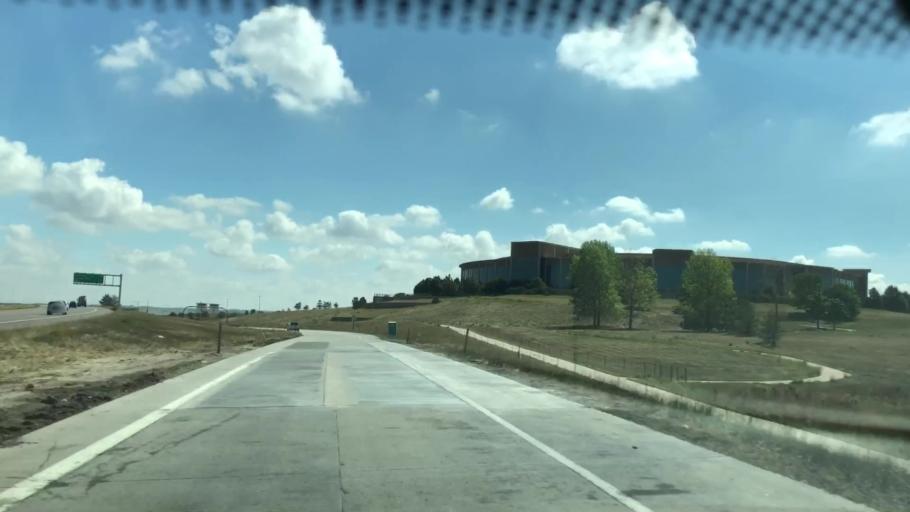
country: US
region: Colorado
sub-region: Douglas County
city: Meridian
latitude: 39.5503
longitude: -104.8465
